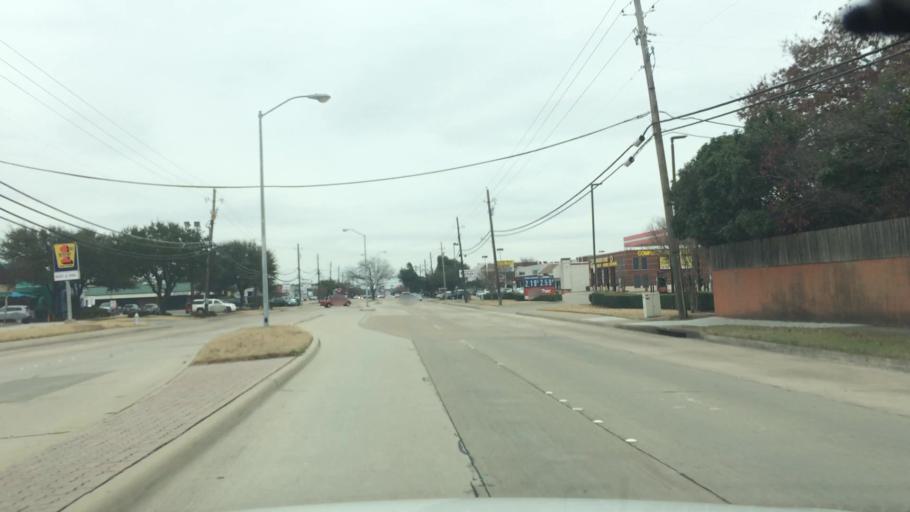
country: US
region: Texas
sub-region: Collin County
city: Plano
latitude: 33.0410
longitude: -96.7375
